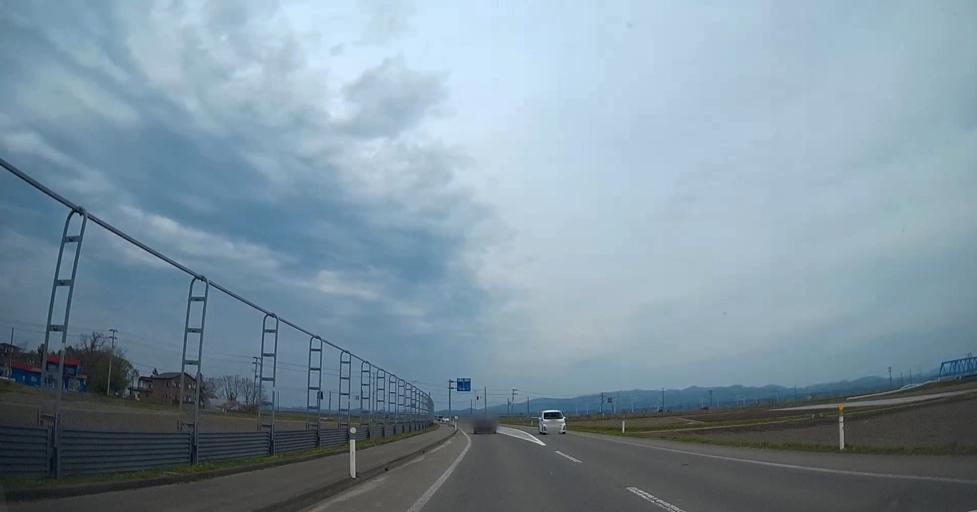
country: JP
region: Aomori
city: Shimokizukuri
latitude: 40.9836
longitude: 140.3766
